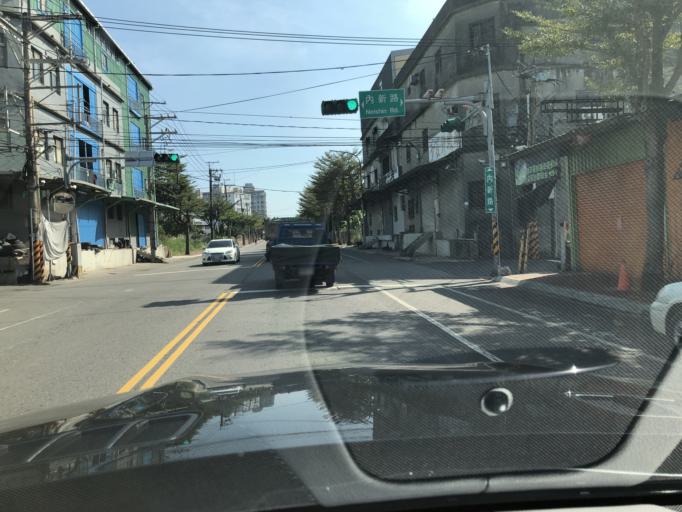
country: TW
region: Taiwan
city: Taoyuan City
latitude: 25.0707
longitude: 121.2886
